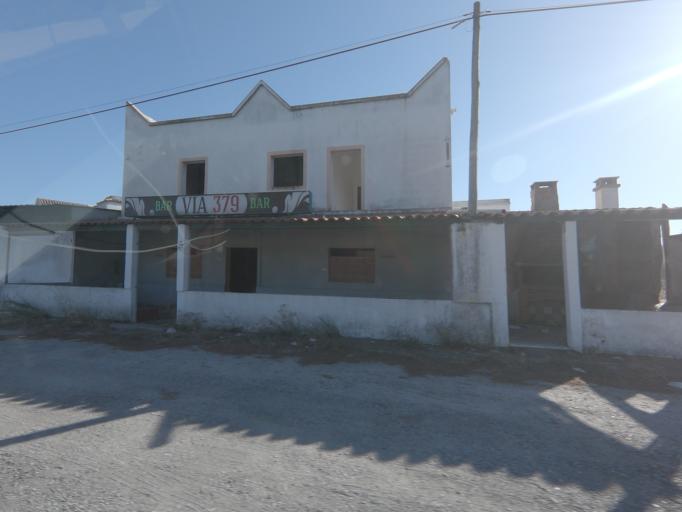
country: PT
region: Setubal
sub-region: Palmela
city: Pinhal Novo
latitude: 38.6203
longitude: -8.9570
